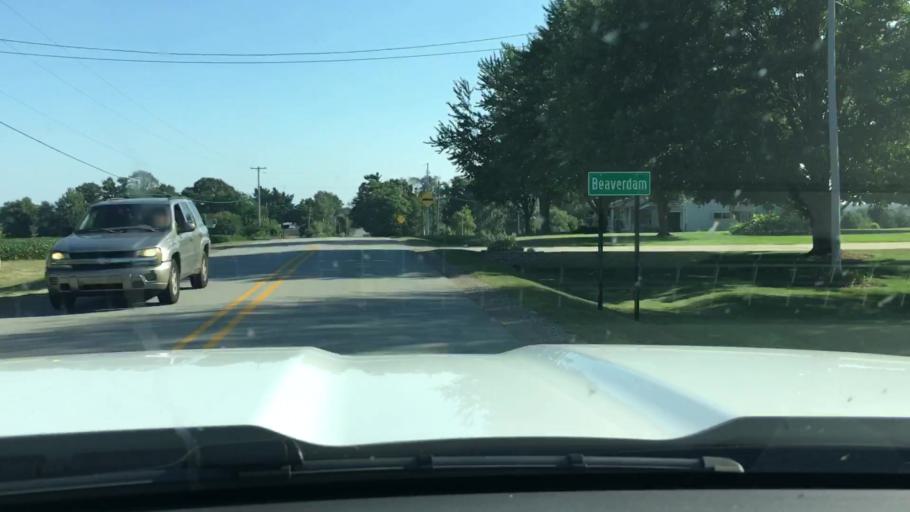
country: US
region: Michigan
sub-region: Ottawa County
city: Zeeland
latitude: 42.8523
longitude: -85.9599
